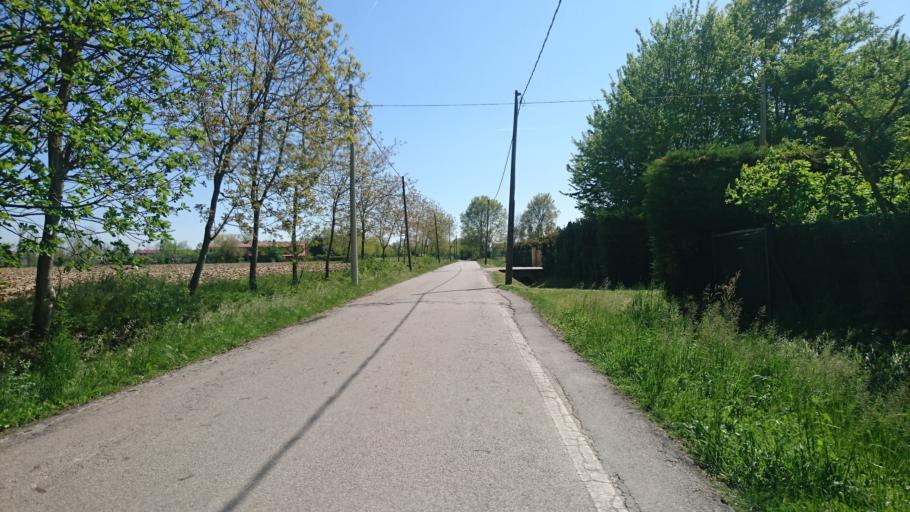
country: IT
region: Veneto
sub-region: Provincia di Venezia
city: Marcon-Gaggio-Colmello
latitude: 45.5863
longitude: 12.2784
